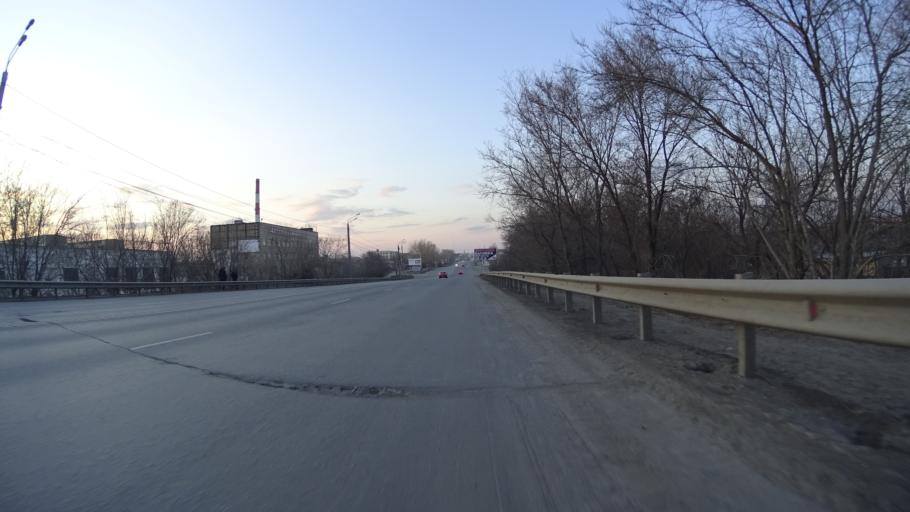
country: RU
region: Chelyabinsk
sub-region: Gorod Chelyabinsk
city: Chelyabinsk
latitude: 55.1038
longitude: 61.3876
